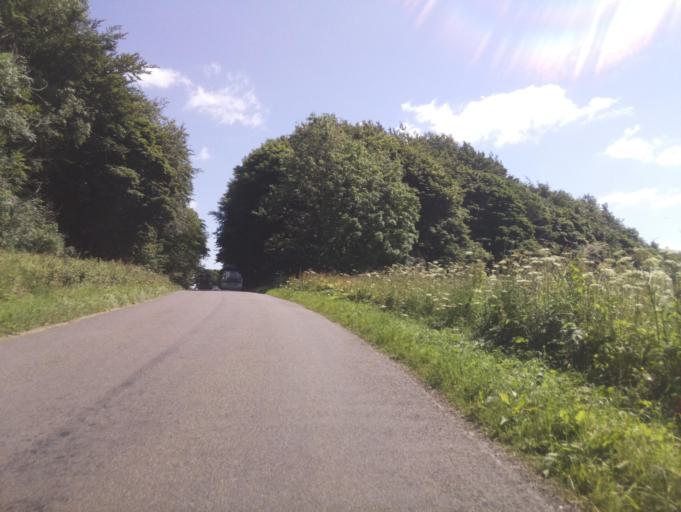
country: GB
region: England
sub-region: Derbyshire
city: Tideswell
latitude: 53.1901
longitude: -1.8066
